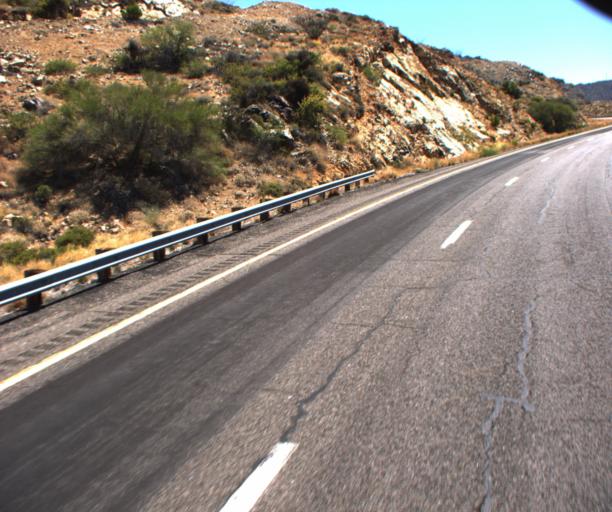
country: US
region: Arizona
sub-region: Yavapai County
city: Congress
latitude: 34.2050
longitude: -112.7954
